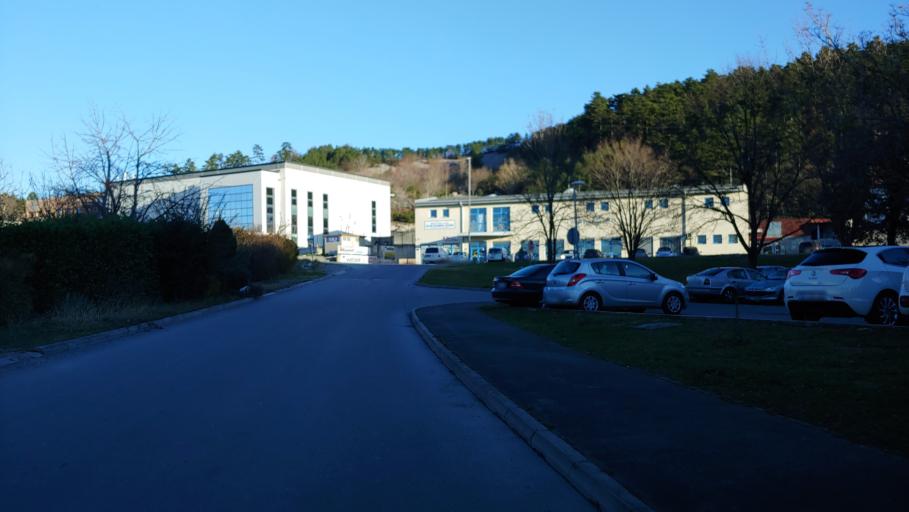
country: SI
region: Sezana
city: Sezana
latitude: 45.7098
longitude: 13.8607
